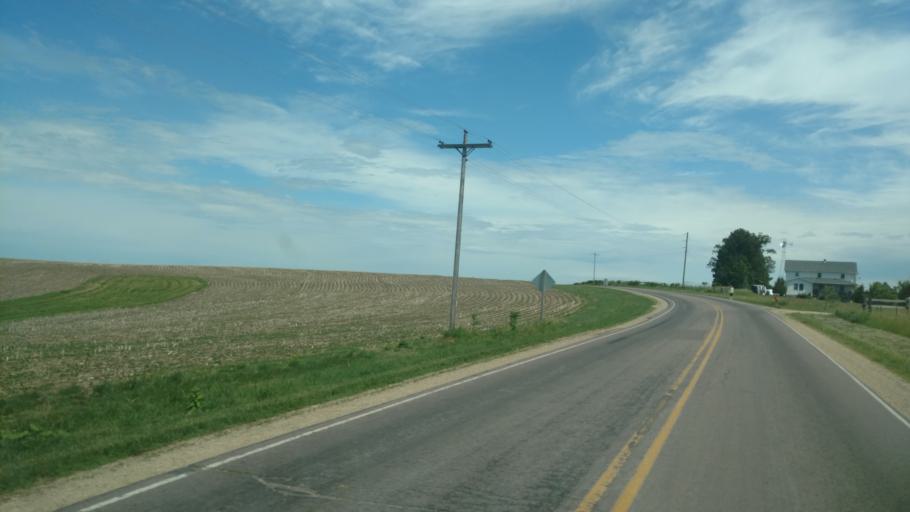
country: US
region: Wisconsin
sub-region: Vernon County
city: Hillsboro
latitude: 43.6471
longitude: -90.4524
